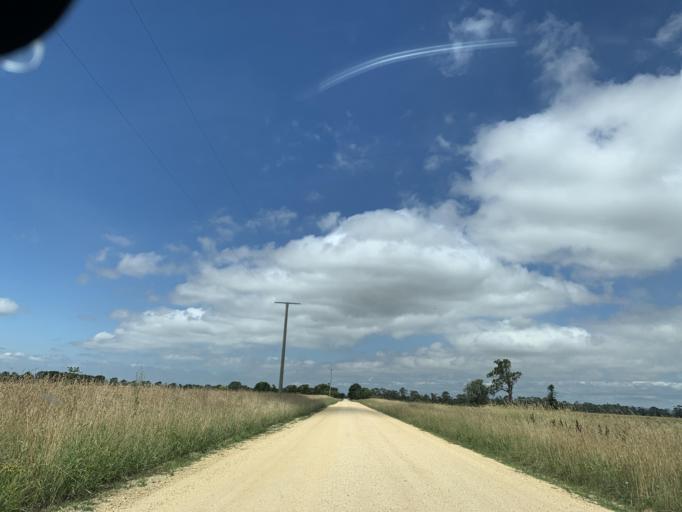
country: AU
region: Victoria
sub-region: Latrobe
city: Traralgon
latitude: -38.0911
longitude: 146.5823
